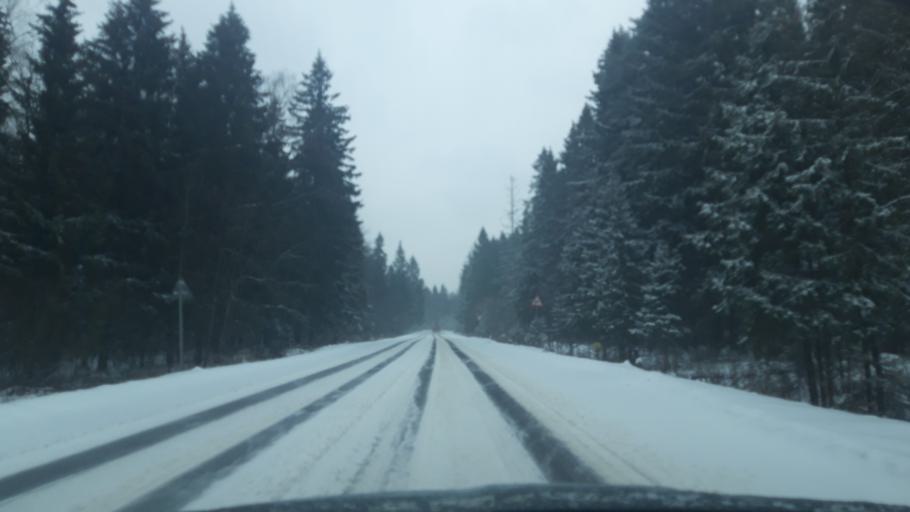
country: RU
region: Moskovskaya
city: Avtopoligon
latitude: 56.2842
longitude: 37.3784
